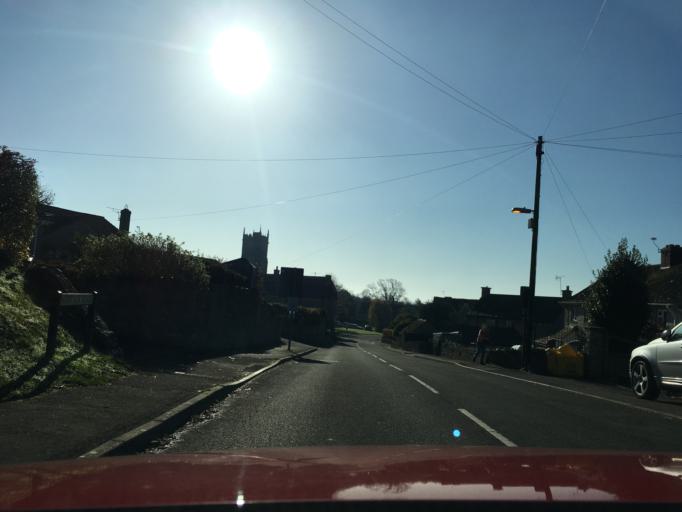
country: GB
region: England
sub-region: Somerset
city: Martock
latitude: 51.0265
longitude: -2.7587
